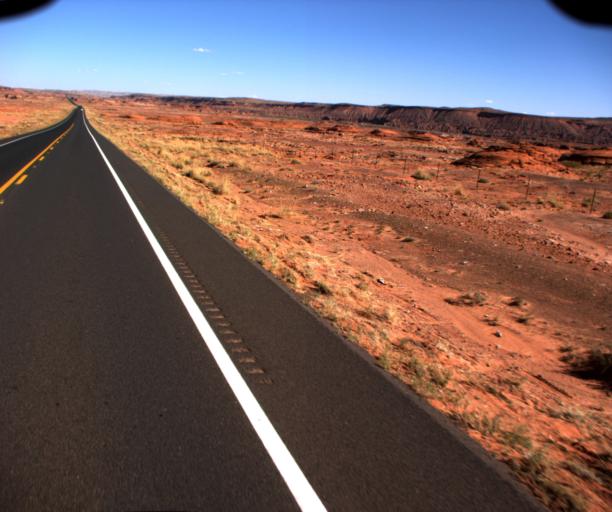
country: US
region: Arizona
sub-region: Coconino County
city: Tuba City
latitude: 36.1008
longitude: -111.3120
